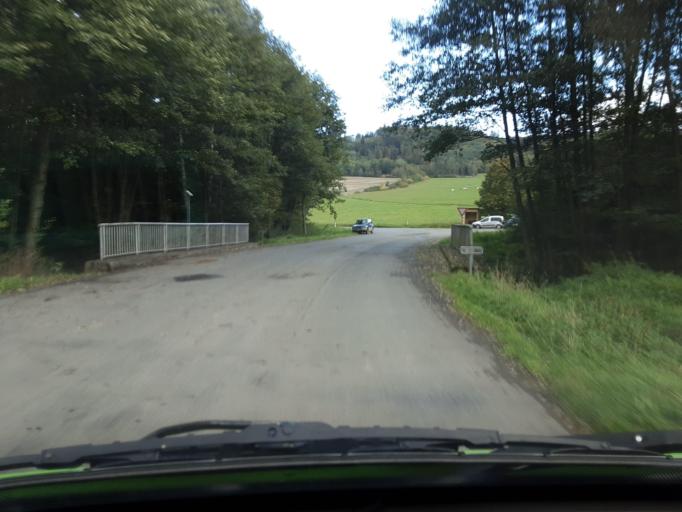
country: CZ
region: Plzensky
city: Janovice nad Uhlavou
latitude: 49.4160
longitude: 13.1672
